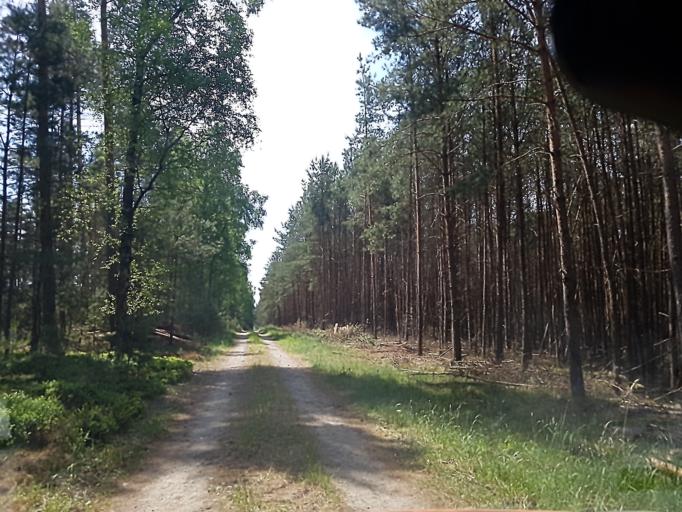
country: DE
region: Brandenburg
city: Gorzke
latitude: 52.1099
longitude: 12.2981
